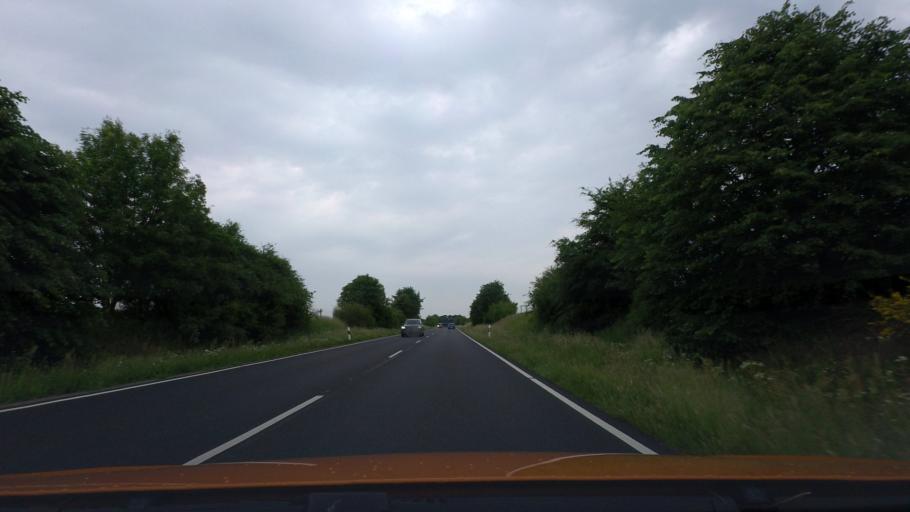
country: DE
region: Lower Saxony
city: Wietzen
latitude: 52.6683
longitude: 9.1039
